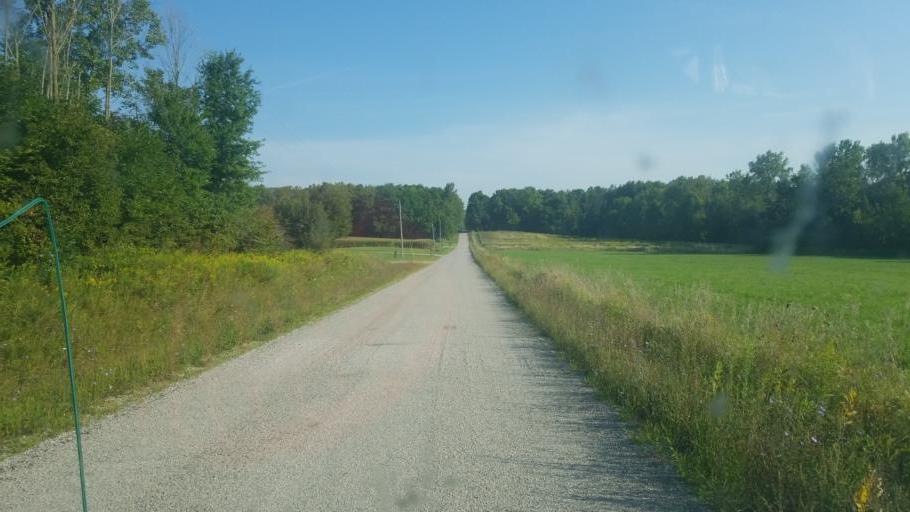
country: US
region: Ohio
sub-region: Ashland County
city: Ashland
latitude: 40.9745
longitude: -82.3404
